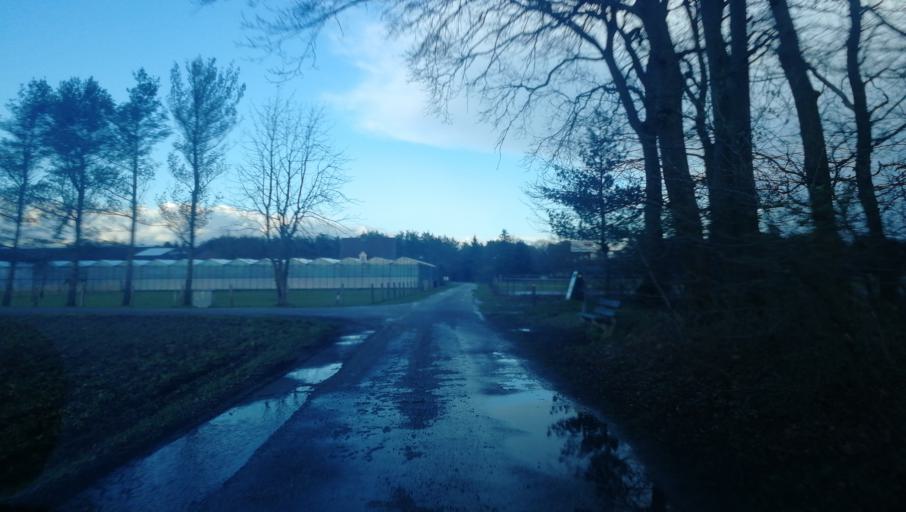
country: NL
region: Limburg
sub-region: Gemeente Peel en Maas
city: Maasbree
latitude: 51.3478
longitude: 6.0520
